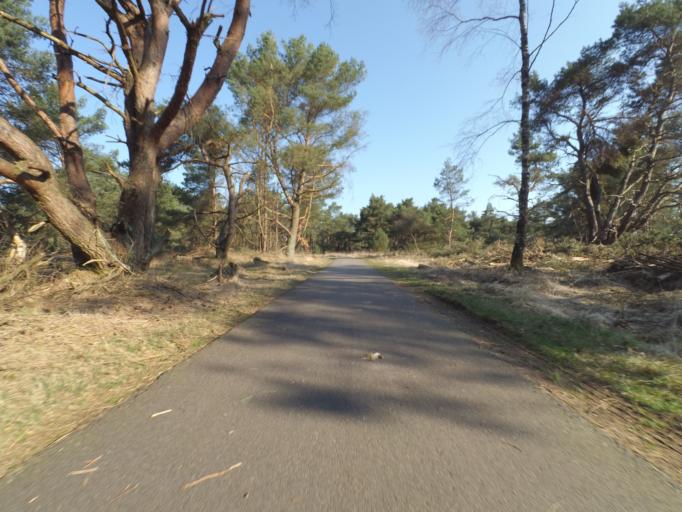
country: NL
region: Gelderland
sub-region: Gemeente Arnhem
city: Hoogkamp
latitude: 52.0775
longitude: 5.8622
